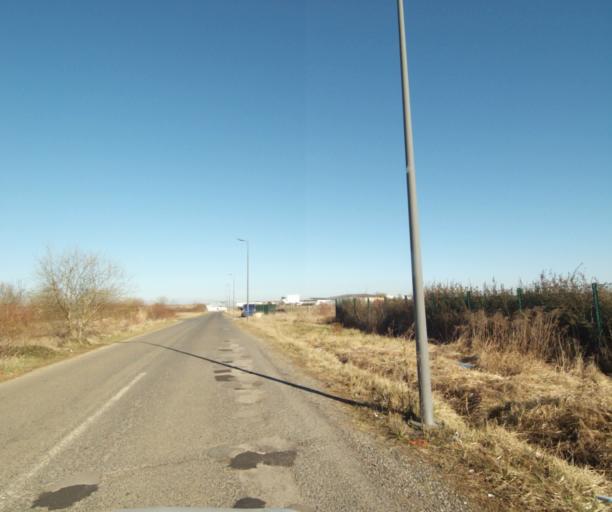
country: FR
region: Lorraine
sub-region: Departement de Meurthe-et-Moselle
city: Tomblaine
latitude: 48.6901
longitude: 6.2176
